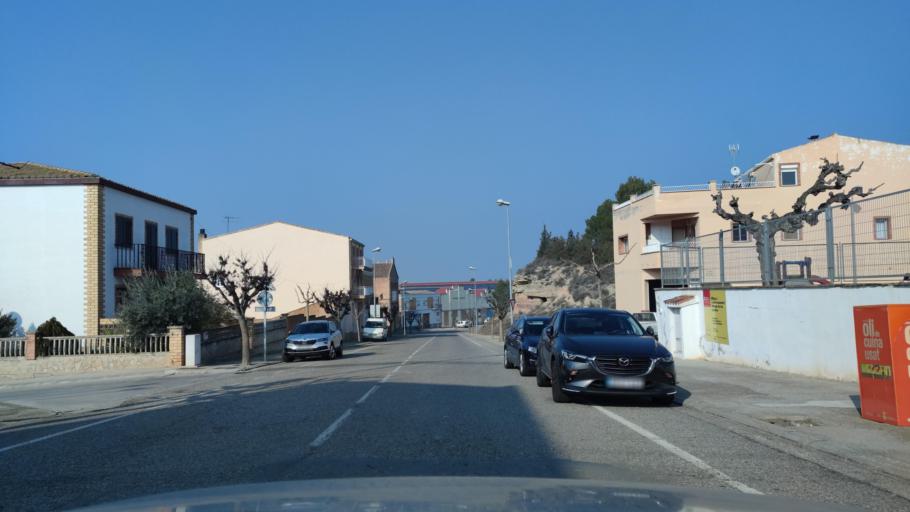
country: ES
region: Catalonia
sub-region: Provincia de Lleida
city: Sunyer
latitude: 41.5608
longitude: 0.5886
